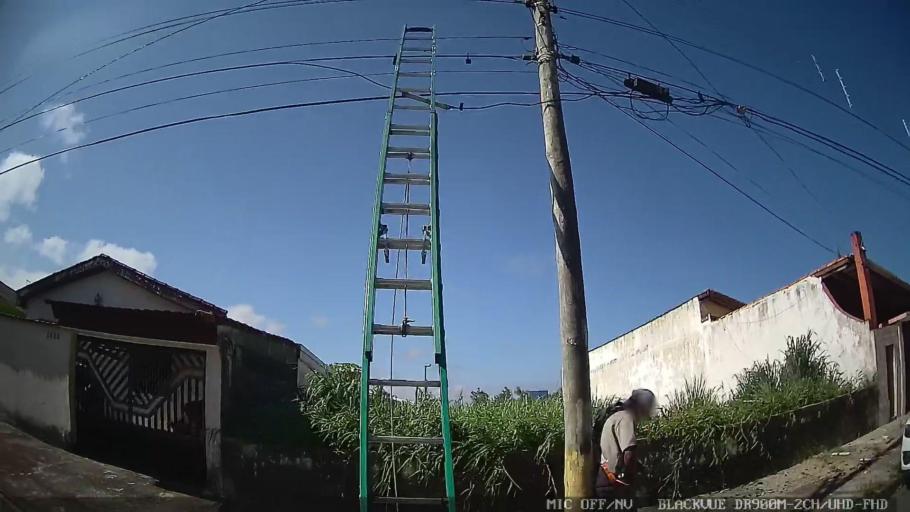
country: BR
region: Sao Paulo
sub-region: Peruibe
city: Peruibe
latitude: -24.3051
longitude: -46.9902
